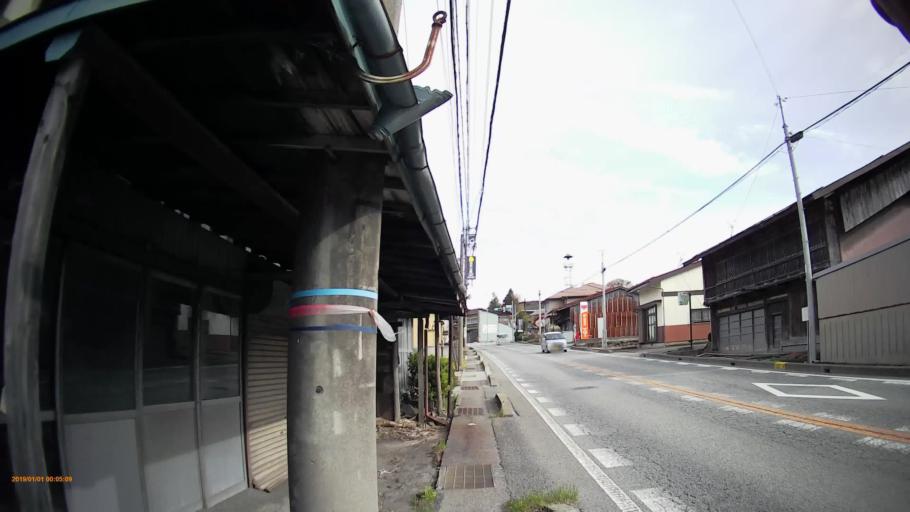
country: JP
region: Nagano
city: Chino
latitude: 35.9487
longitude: 138.1876
